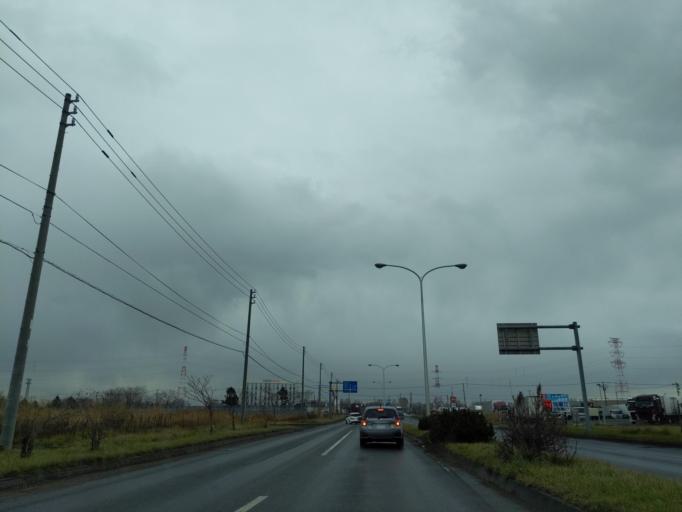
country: JP
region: Hokkaido
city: Ishikari
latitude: 43.1865
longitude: 141.3080
